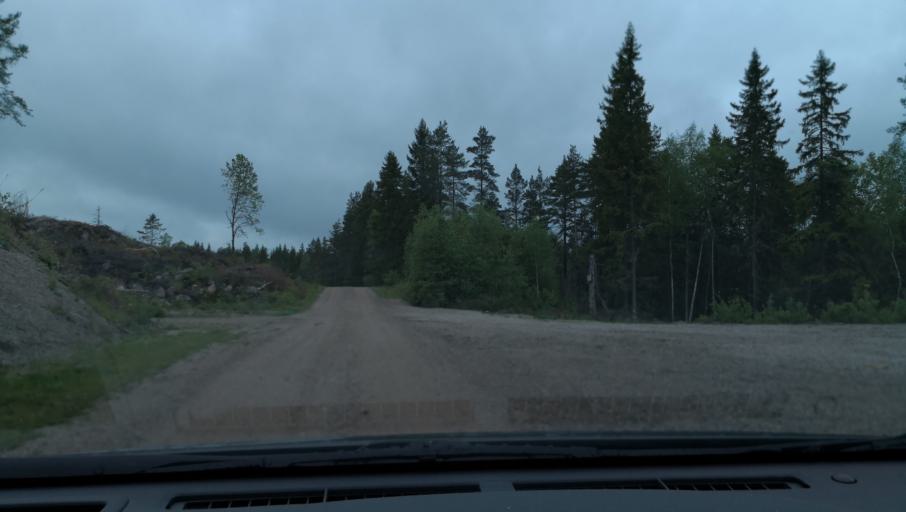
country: SE
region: Uppsala
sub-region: Enkopings Kommun
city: Orsundsbro
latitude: 59.9415
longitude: 17.3113
